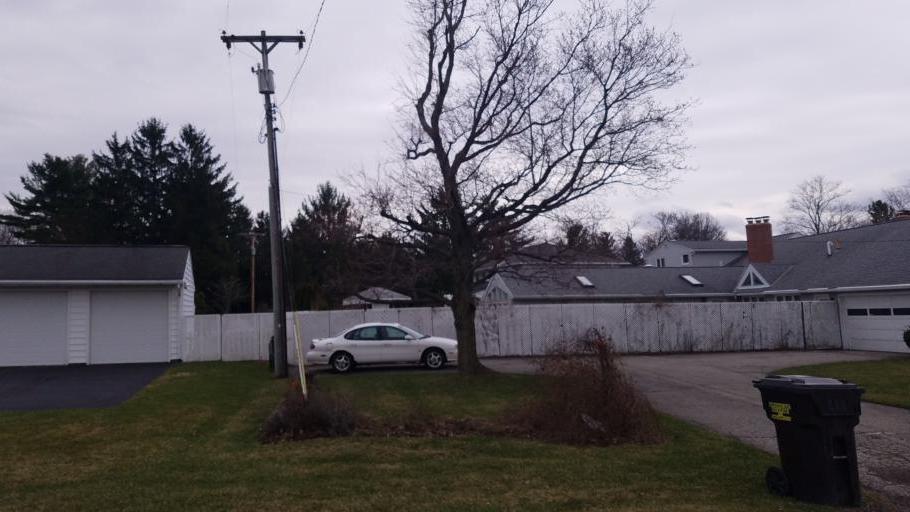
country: US
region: Ohio
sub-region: Richland County
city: Mansfield
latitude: 40.7314
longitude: -82.5439
